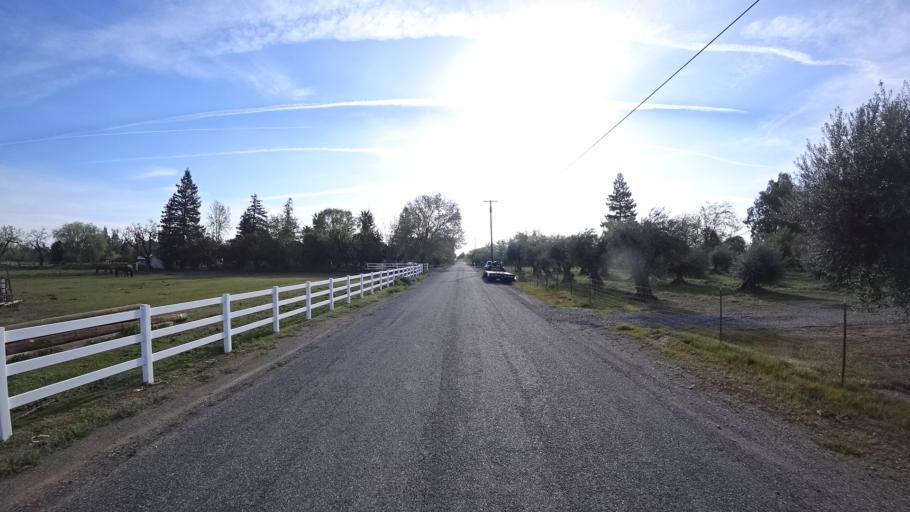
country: US
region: California
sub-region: Glenn County
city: Orland
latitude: 39.7151
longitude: -122.2189
